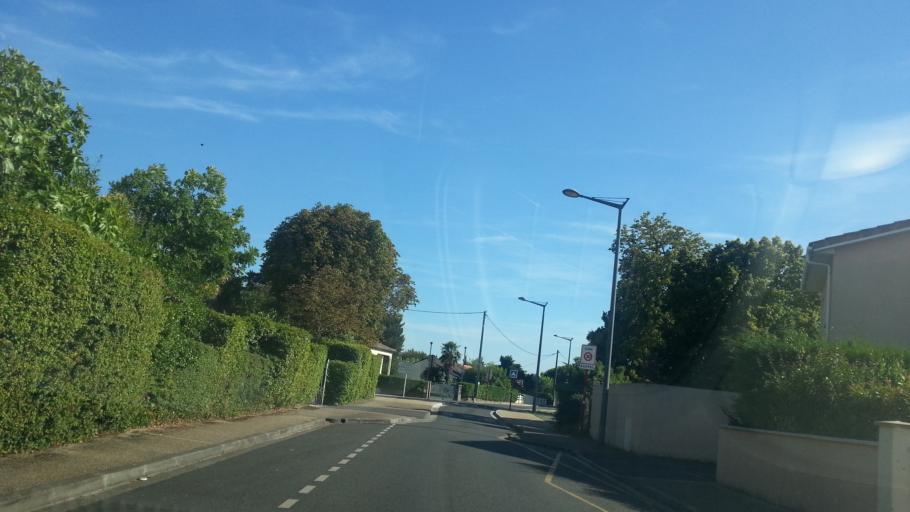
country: FR
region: Aquitaine
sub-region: Departement de la Gironde
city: Bassens
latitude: 44.8978
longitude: -0.5162
